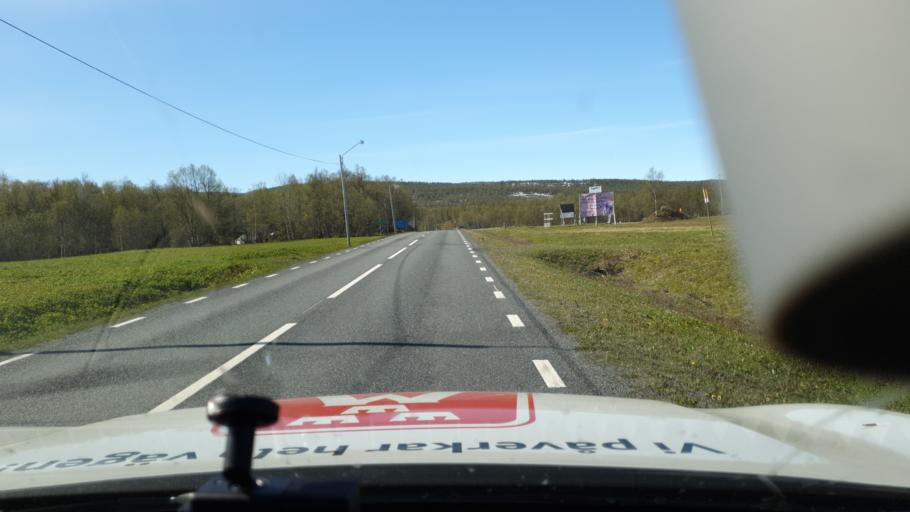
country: NO
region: Nordland
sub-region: Rana
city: Mo i Rana
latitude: 65.7457
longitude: 15.0898
